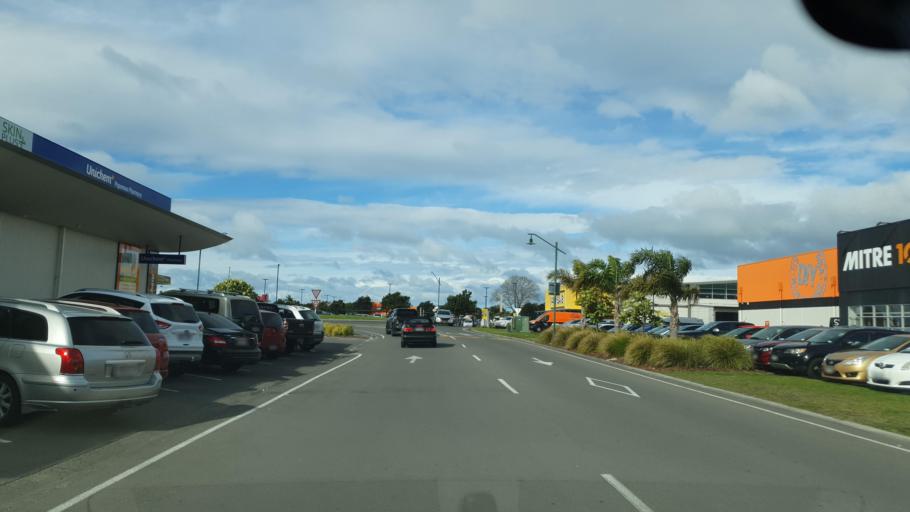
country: NZ
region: Bay of Plenty
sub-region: Tauranga City
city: Tauranga
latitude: -37.7015
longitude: 176.2820
